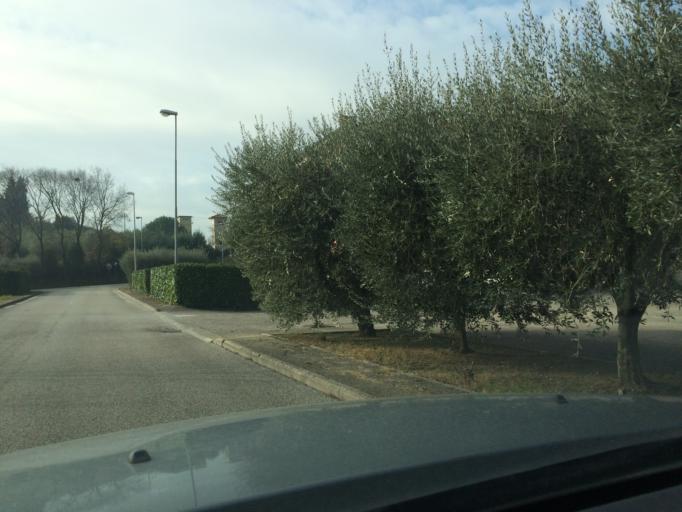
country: IT
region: Umbria
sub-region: Provincia di Perugia
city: Via Lippia
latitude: 43.1006
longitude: 12.4910
